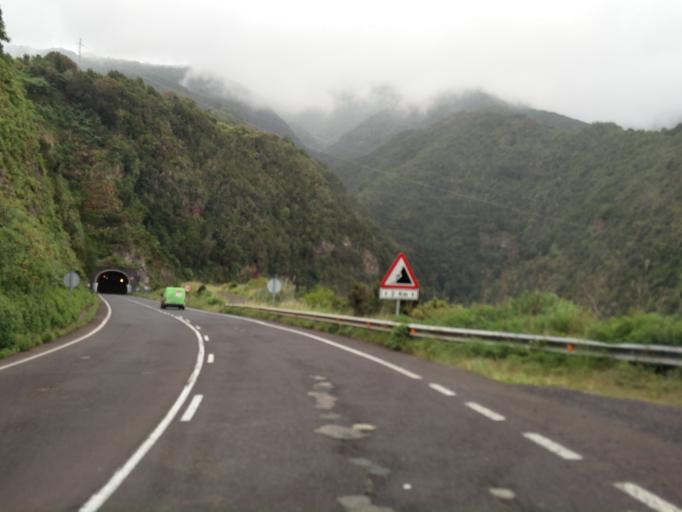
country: ES
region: Canary Islands
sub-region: Provincia de Santa Cruz de Tenerife
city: Garachico
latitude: 28.7684
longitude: -17.7639
